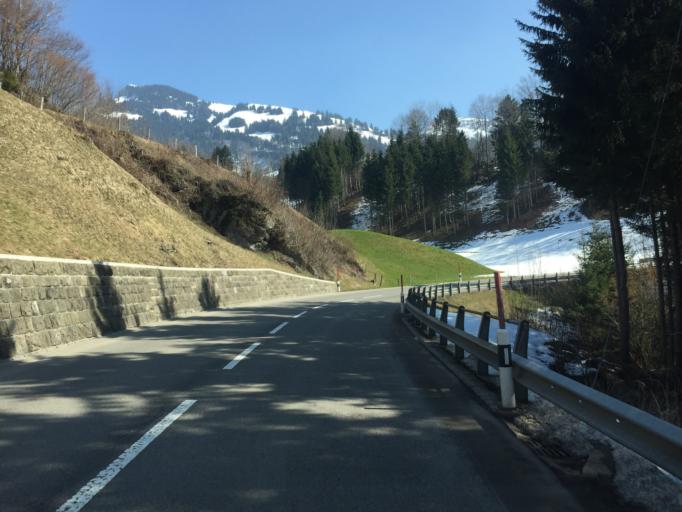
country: CH
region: Saint Gallen
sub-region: Wahlkreis Toggenburg
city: Krummenau
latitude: 47.2196
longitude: 9.2089
